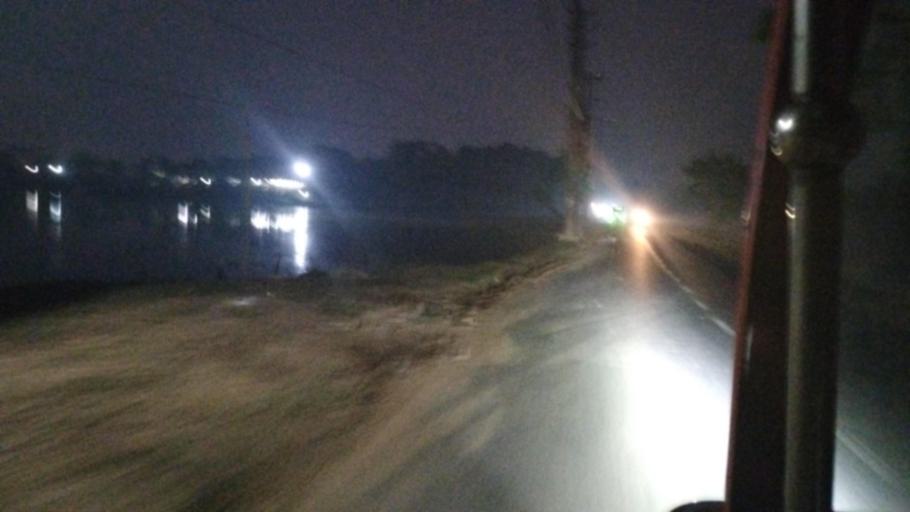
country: BD
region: Dhaka
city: Gafargaon
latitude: 24.4009
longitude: 90.3649
